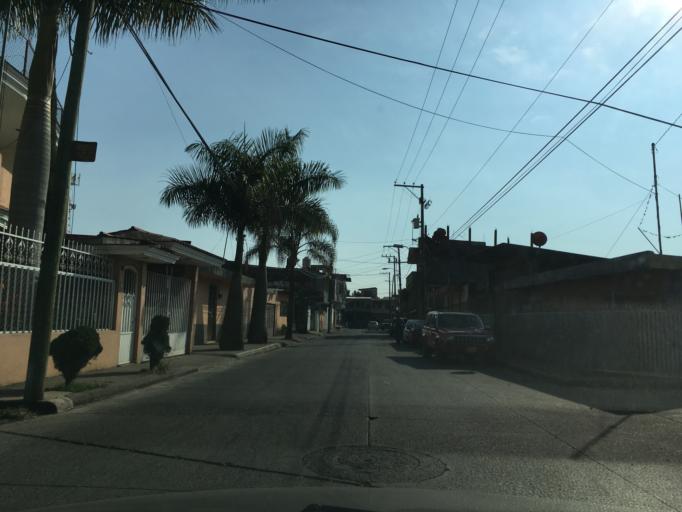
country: MX
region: Michoacan
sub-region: Uruapan
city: Uruapan
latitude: 19.4063
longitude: -102.0678
